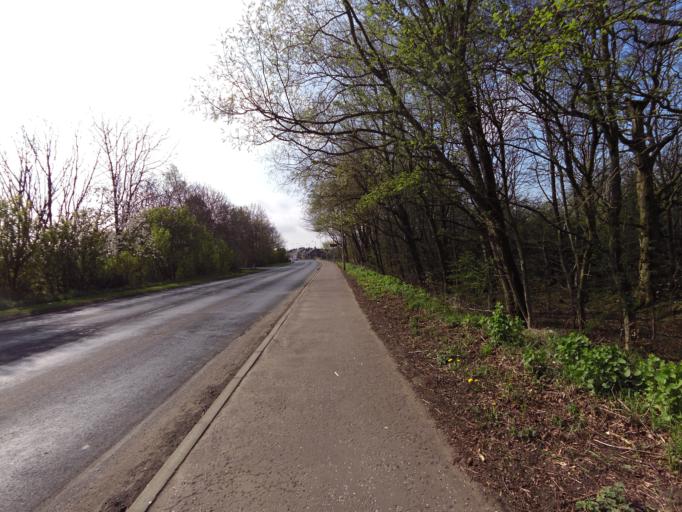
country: GB
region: Scotland
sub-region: Fife
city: Thornton
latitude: 56.1721
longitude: -3.1460
